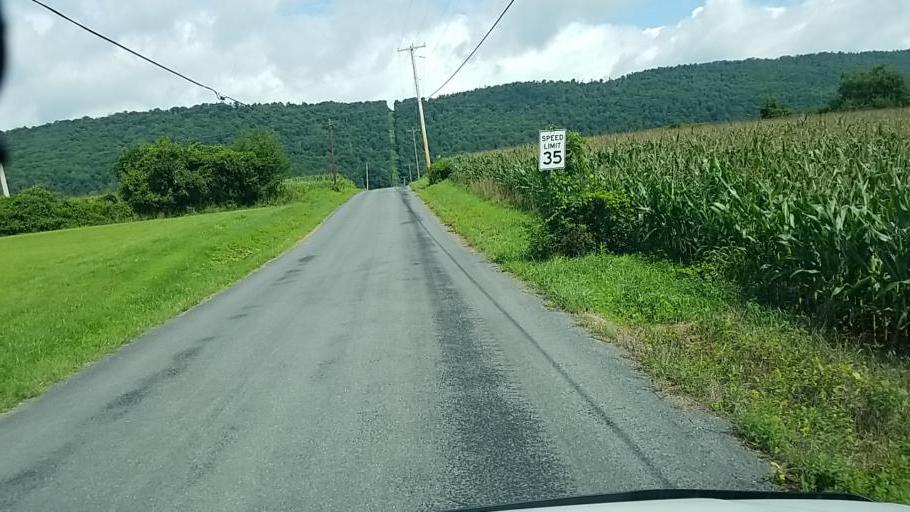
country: US
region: Pennsylvania
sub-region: Dauphin County
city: Millersburg
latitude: 40.5740
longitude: -76.9312
